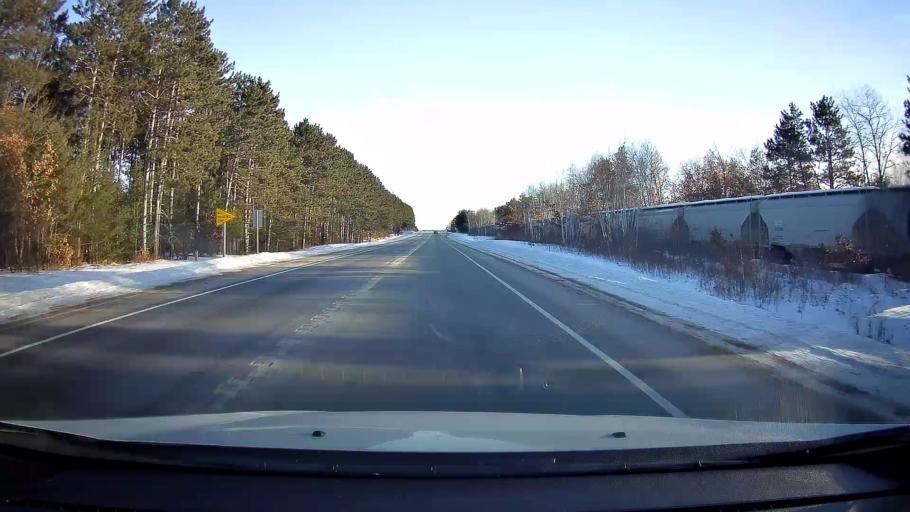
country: US
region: Wisconsin
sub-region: Washburn County
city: Spooner
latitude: 45.8456
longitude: -91.8708
